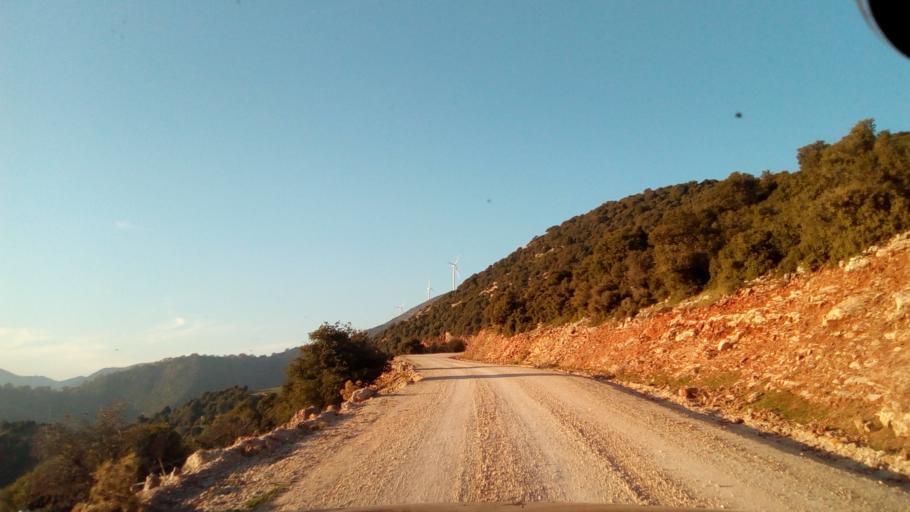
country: GR
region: West Greece
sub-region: Nomos Aitolias kai Akarnanias
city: Nafpaktos
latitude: 38.4392
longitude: 21.8471
